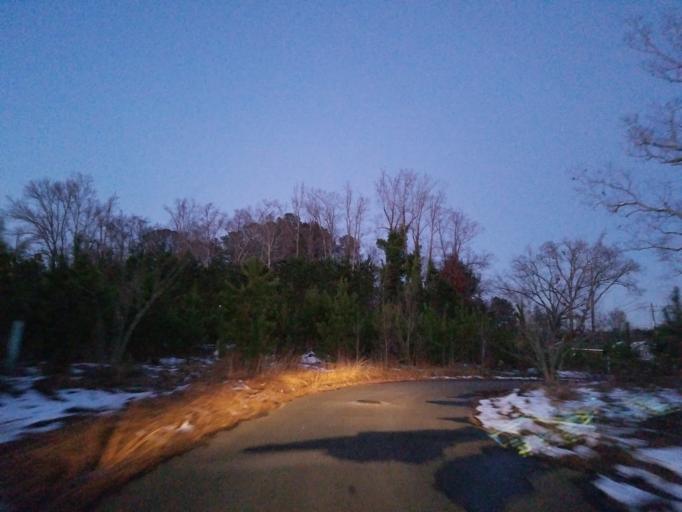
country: US
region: Georgia
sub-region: Cherokee County
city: Ball Ground
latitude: 34.3289
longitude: -84.3874
